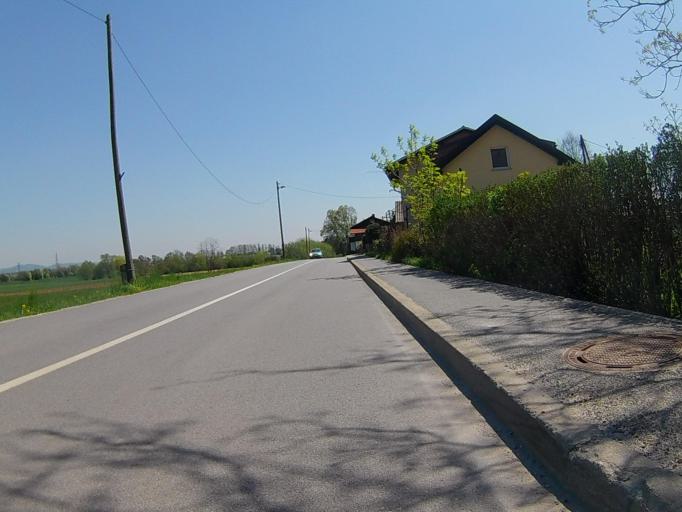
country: SI
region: Maribor
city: Razvanje
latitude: 46.5074
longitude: 15.6399
